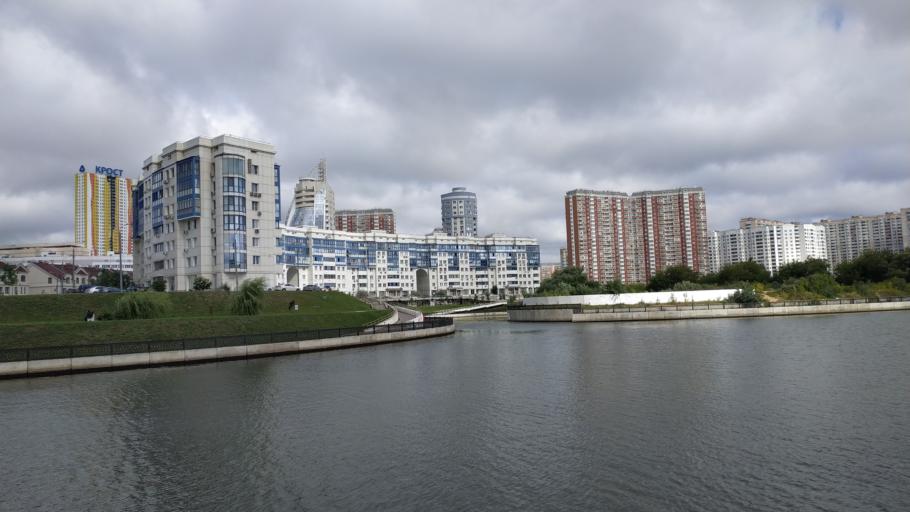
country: RU
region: Moskovskaya
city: Pavshino
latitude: 55.8105
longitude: 37.3726
